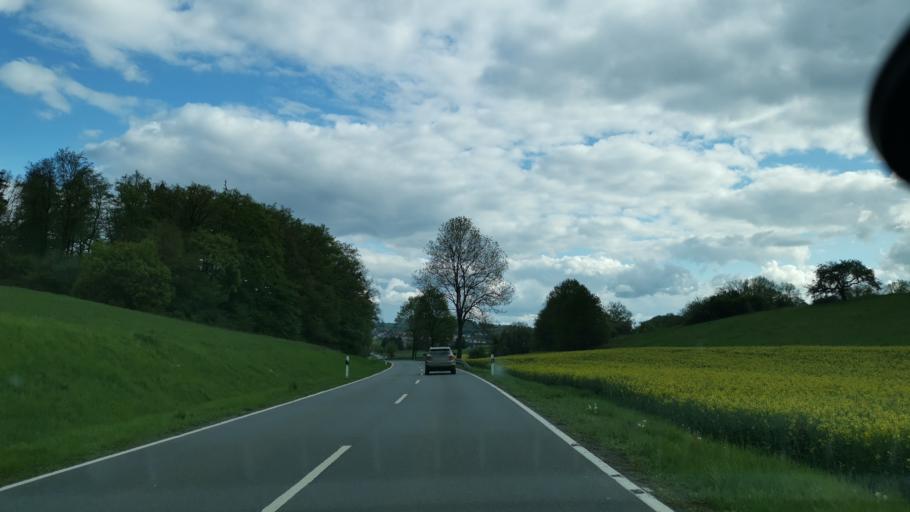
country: DE
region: Baden-Wuerttemberg
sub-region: Karlsruhe Region
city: Osterburken
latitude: 49.4461
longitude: 9.4268
